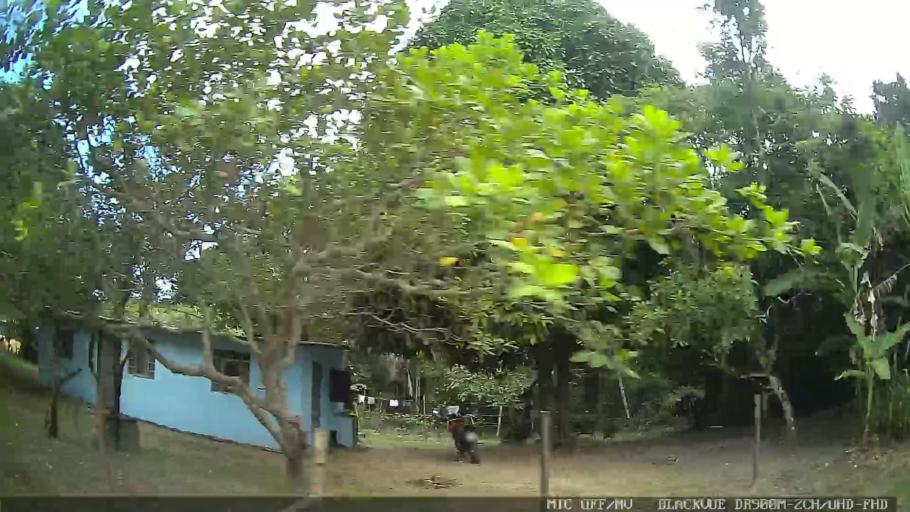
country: BR
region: Sao Paulo
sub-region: Iguape
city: Iguape
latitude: -24.6535
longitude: -47.4042
